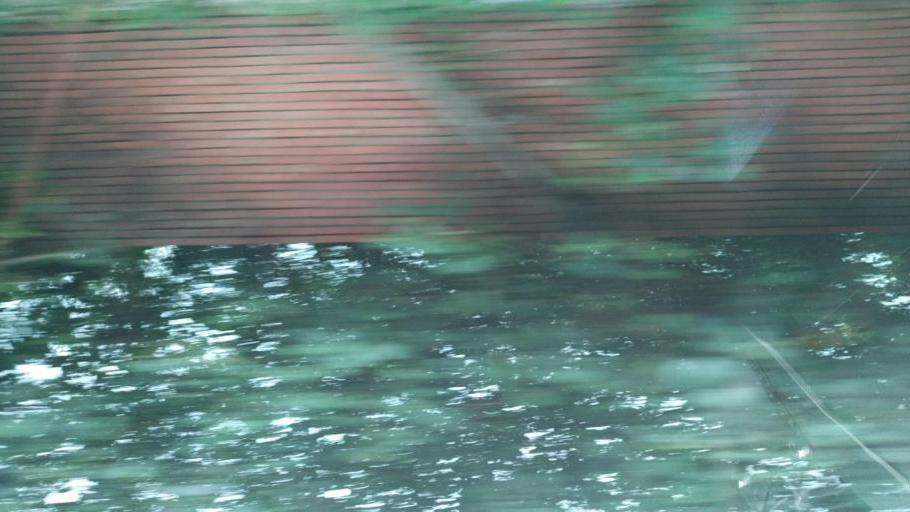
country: TW
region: Taiwan
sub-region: Keelung
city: Keelung
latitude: 25.2143
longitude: 121.6475
